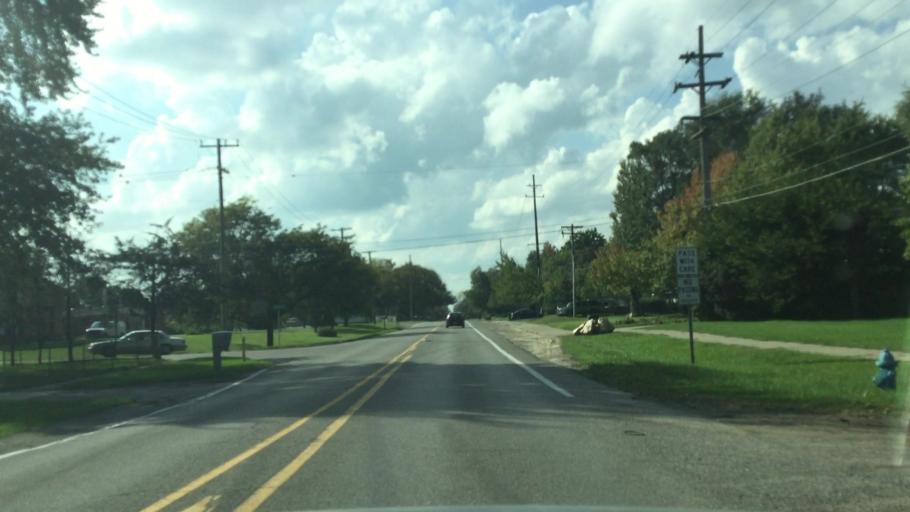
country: US
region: Michigan
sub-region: Oakland County
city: Waterford
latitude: 42.6531
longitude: -83.3878
